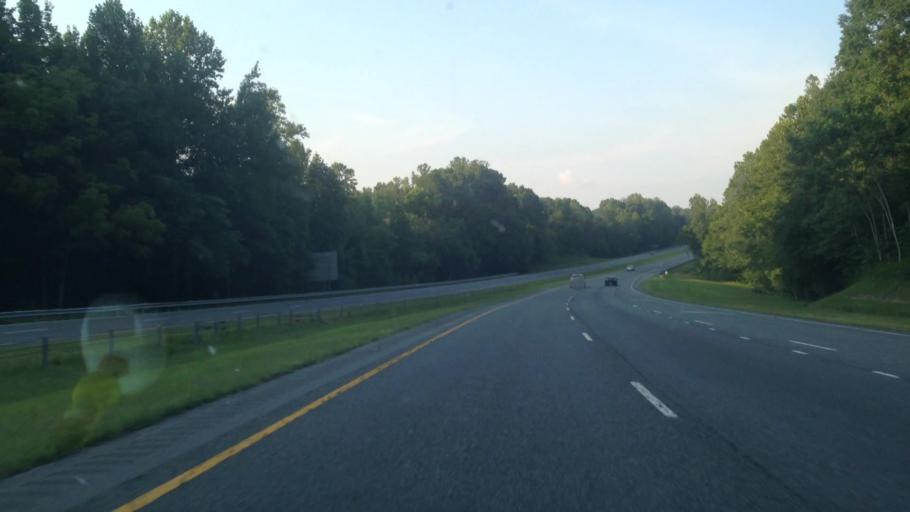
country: US
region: North Carolina
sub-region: Rockingham County
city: Reidsville
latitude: 36.4060
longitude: -79.5959
